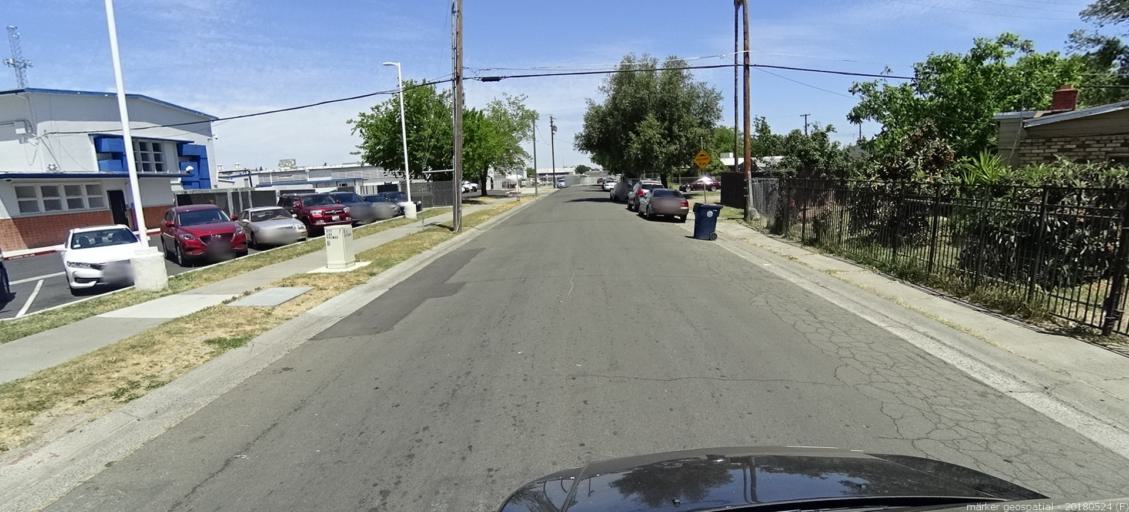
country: US
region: California
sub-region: Sacramento County
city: Sacramento
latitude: 38.6188
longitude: -121.4524
